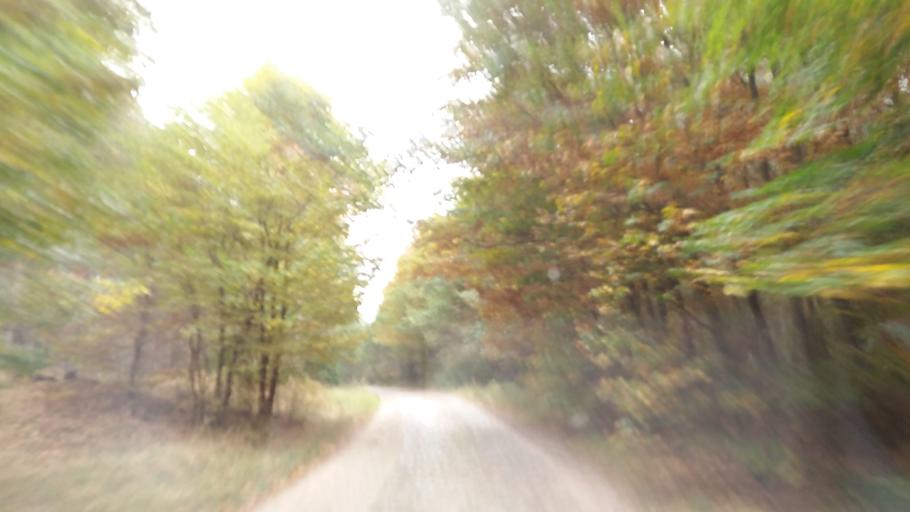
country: PL
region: West Pomeranian Voivodeship
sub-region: Powiat mysliborski
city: Barlinek
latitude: 52.9394
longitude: 15.2545
